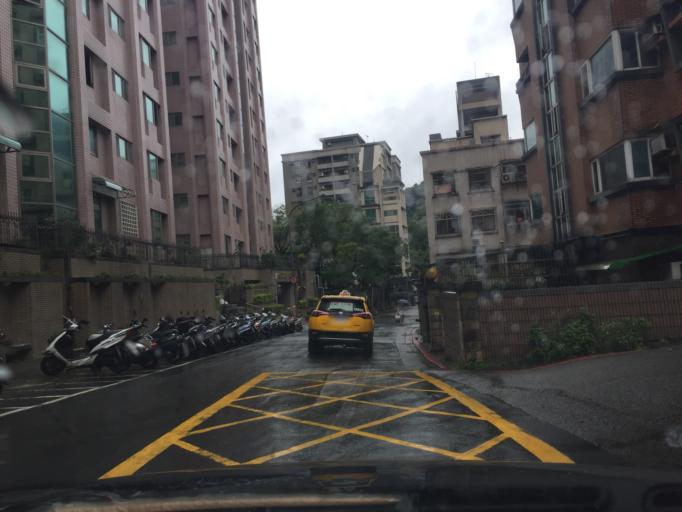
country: TW
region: Taipei
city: Taipei
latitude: 25.0802
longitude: 121.5976
